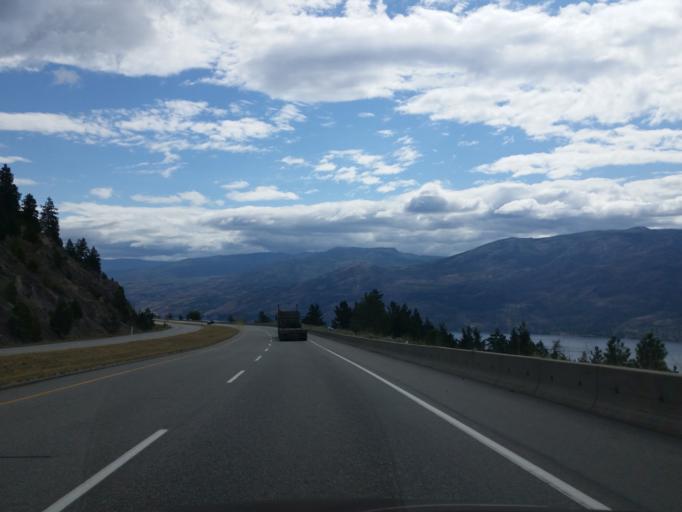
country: CA
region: British Columbia
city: Peachland
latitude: 49.8016
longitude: -119.7058
